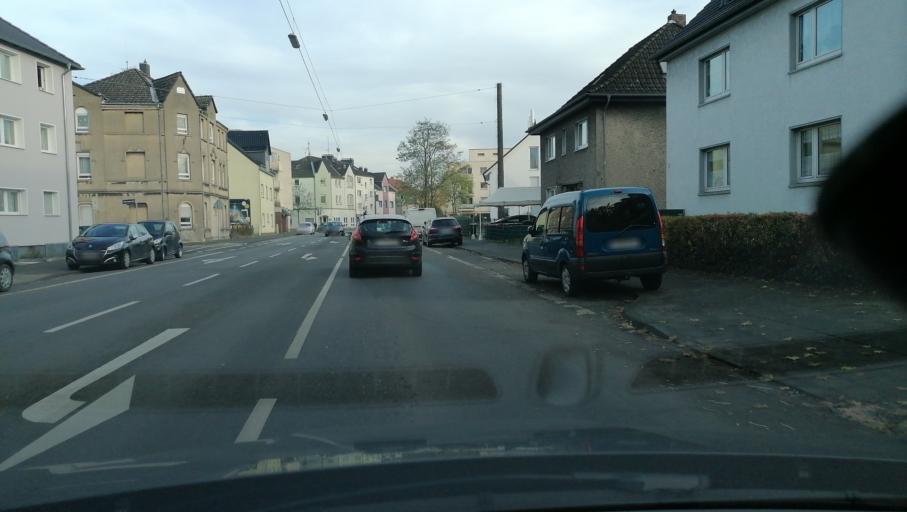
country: DE
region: North Rhine-Westphalia
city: Castrop-Rauxel
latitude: 51.5890
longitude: 7.3042
